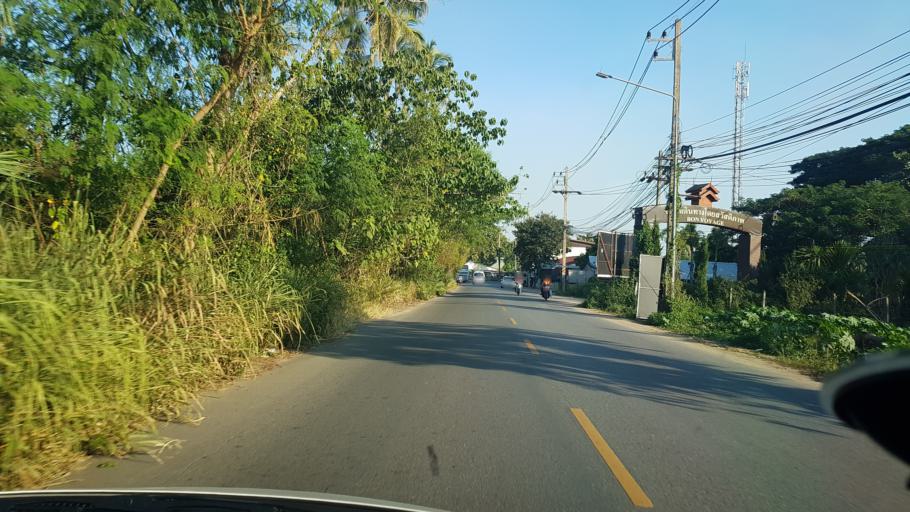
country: TH
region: Chiang Rai
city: Chiang Rai
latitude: 19.9295
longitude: 99.8274
